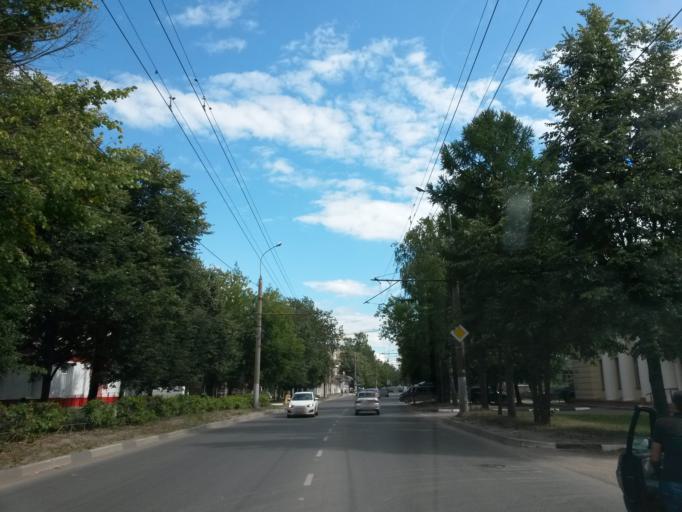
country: RU
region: Ivanovo
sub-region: Gorod Ivanovo
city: Ivanovo
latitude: 56.9862
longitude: 40.9902
